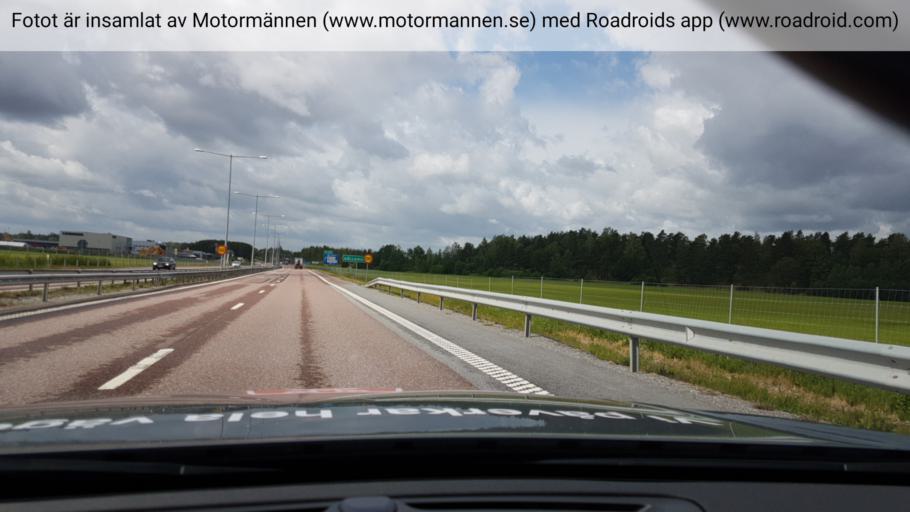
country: SE
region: Vaestmanland
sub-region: Vasteras
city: Tillberga
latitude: 59.6150
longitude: 16.6448
